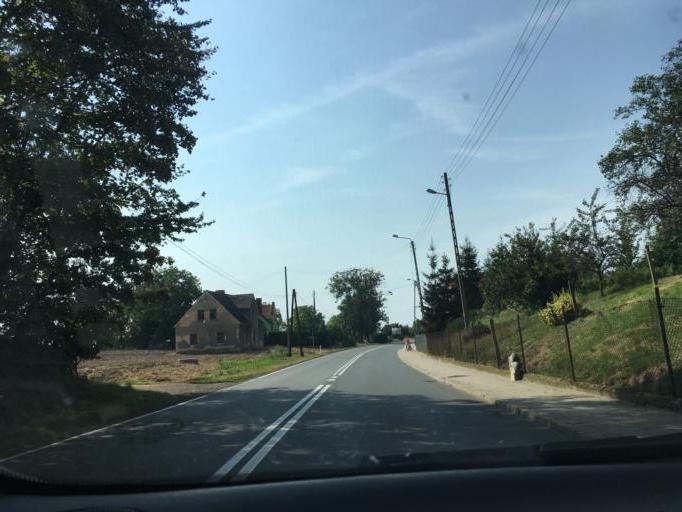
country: PL
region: Opole Voivodeship
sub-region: Powiat nyski
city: Nysa
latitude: 50.4254
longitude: 17.4319
